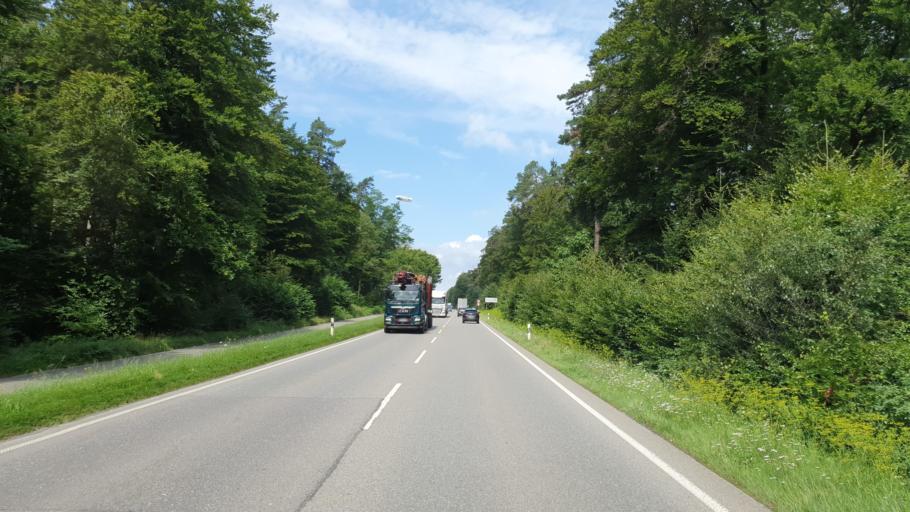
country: DE
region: Baden-Wuerttemberg
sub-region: Tuebingen Region
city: Eriskirch
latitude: 47.6217
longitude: 9.5586
